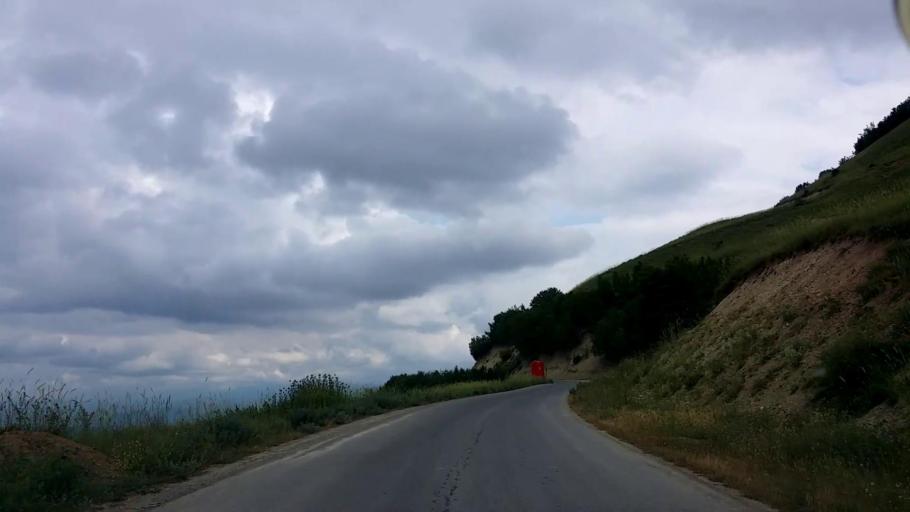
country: IR
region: Mazandaran
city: Chalus
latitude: 36.5437
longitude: 51.2716
